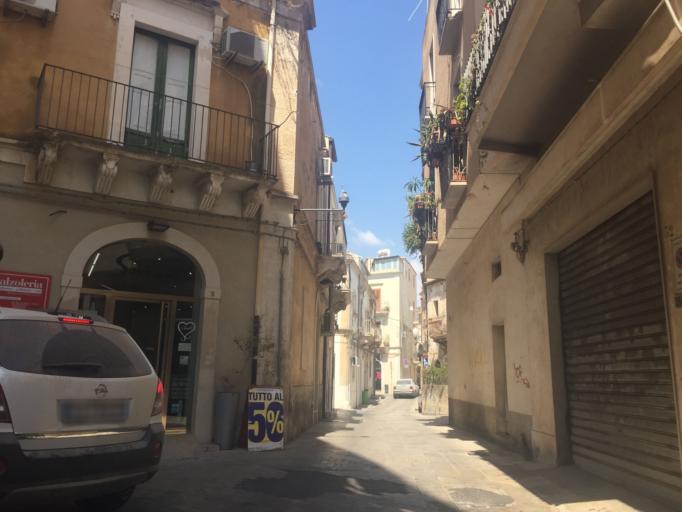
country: IT
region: Sicily
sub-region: Ragusa
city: Scicli
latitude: 36.7919
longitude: 14.7054
